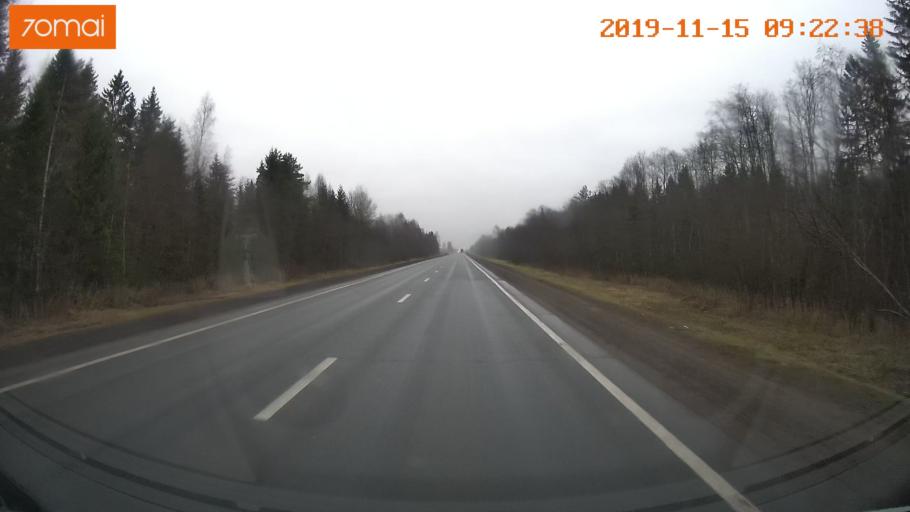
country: RU
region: Vologda
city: Tonshalovo
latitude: 59.2985
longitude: 38.0944
